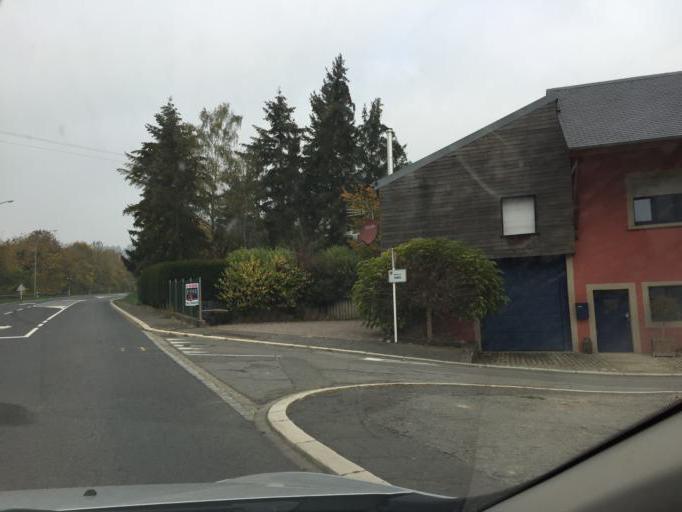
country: LU
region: Luxembourg
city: Moutfort
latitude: 49.5763
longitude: 6.2739
